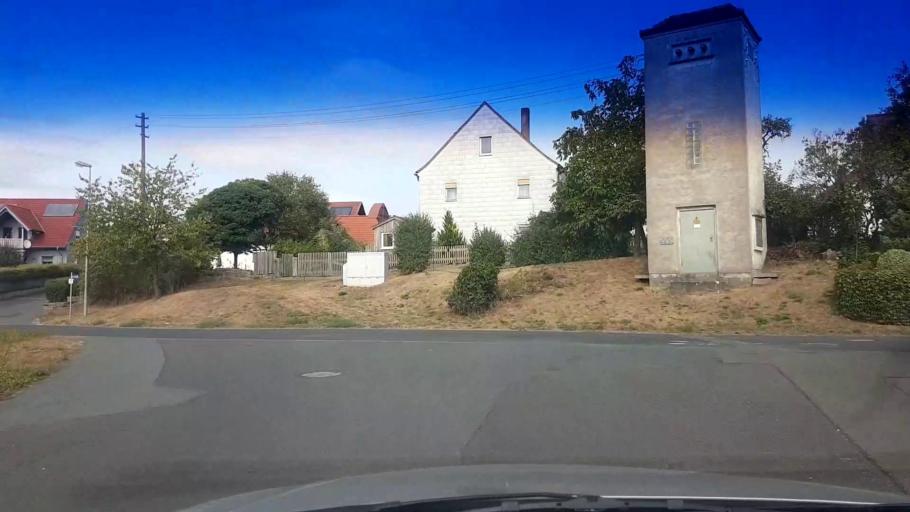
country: DE
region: Bavaria
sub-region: Upper Franconia
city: Pettstadt
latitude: 49.7981
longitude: 10.9257
